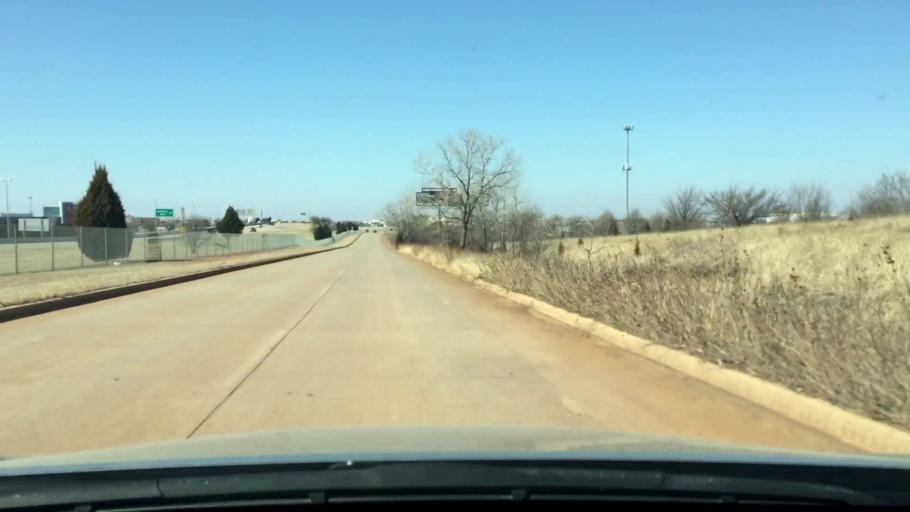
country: US
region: Oklahoma
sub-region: Oklahoma County
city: The Village
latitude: 35.6048
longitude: -97.5233
